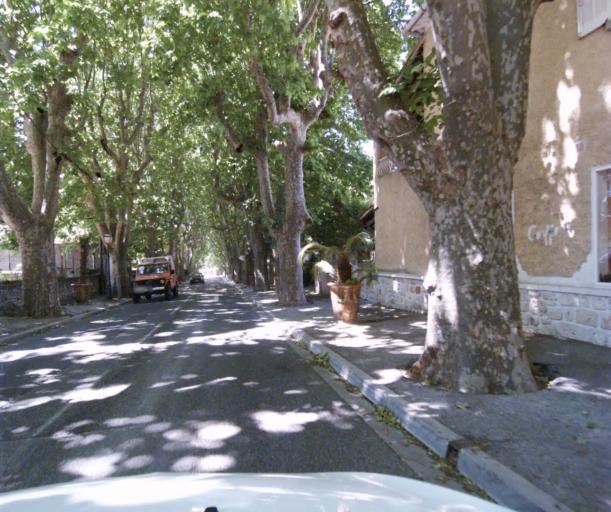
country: FR
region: Provence-Alpes-Cote d'Azur
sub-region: Departement du Var
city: Le Revest-les-Eaux
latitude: 43.1765
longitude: 5.9254
